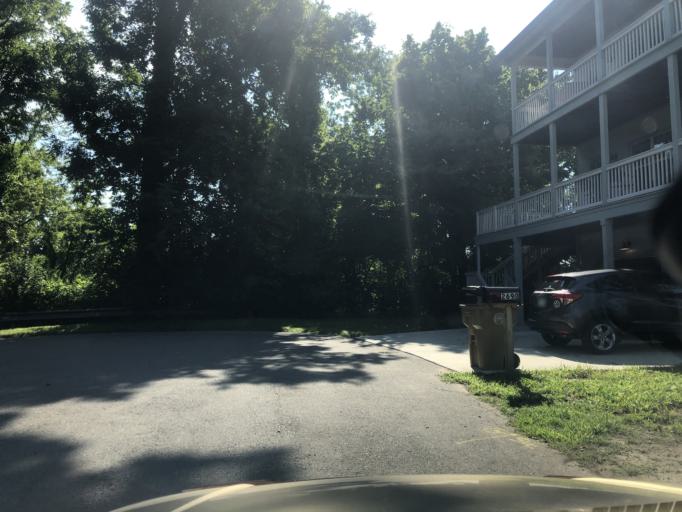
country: US
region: Tennessee
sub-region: Davidson County
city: Lakewood
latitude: 36.2436
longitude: -86.7049
